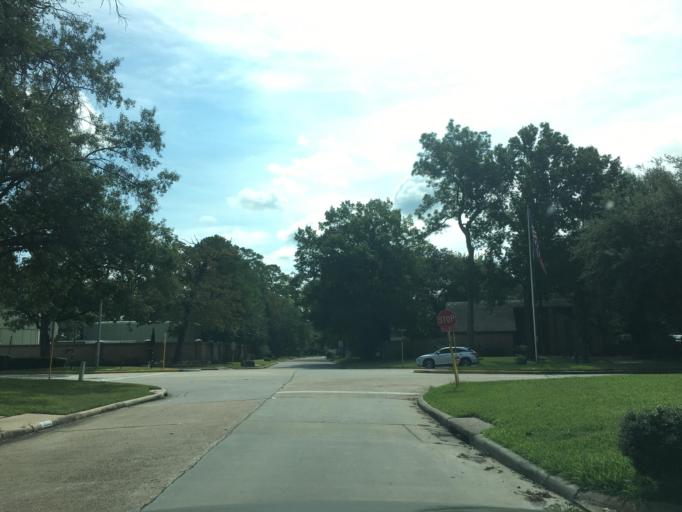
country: US
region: Texas
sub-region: Harris County
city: Spring
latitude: 30.0494
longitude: -95.4390
